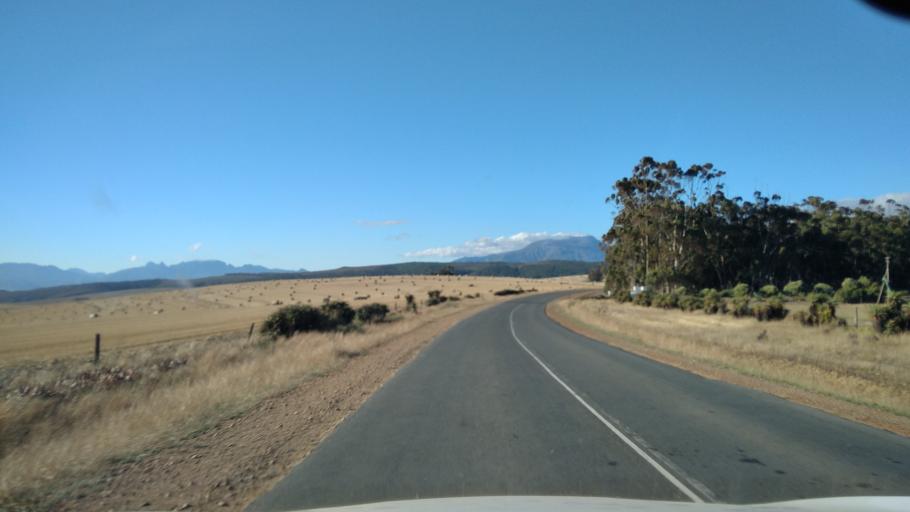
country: ZA
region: Western Cape
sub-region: Overberg District Municipality
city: Caledon
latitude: -34.1413
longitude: 19.2967
